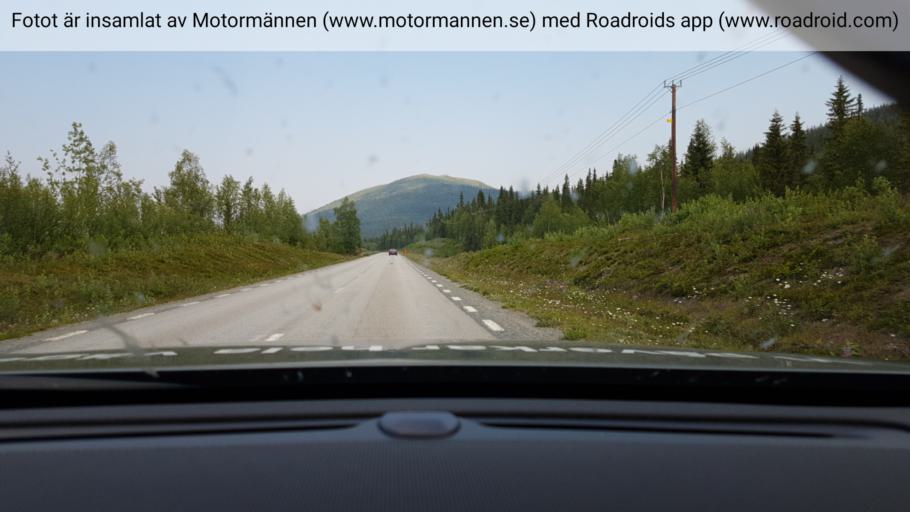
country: SE
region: Vaesterbotten
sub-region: Vilhelmina Kommun
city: Sjoberg
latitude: 65.5253
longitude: 15.6211
